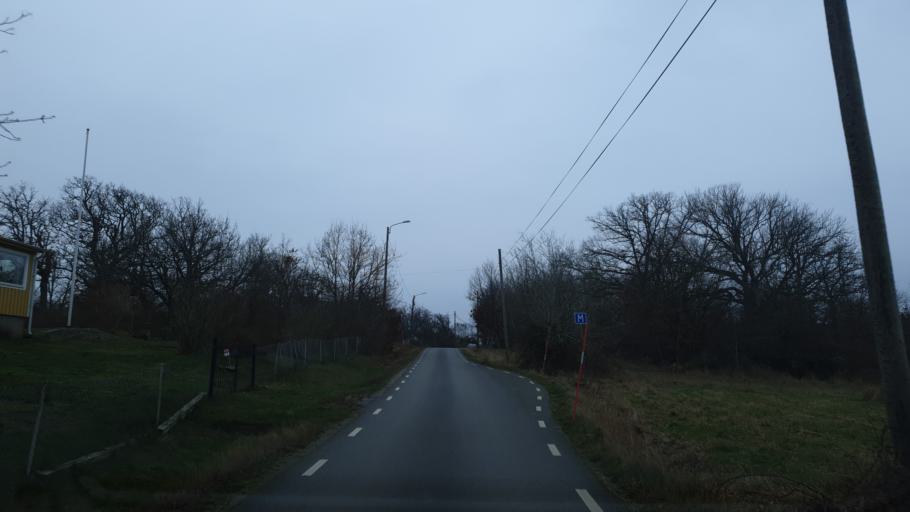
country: SE
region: Blekinge
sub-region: Karlskrona Kommun
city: Karlskrona
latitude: 56.1284
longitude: 15.6194
